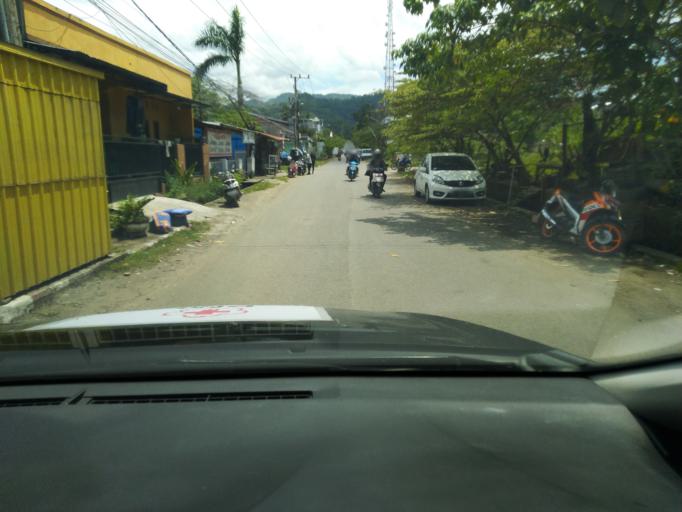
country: ID
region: Sulawesi Barat
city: Mamuju
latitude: -2.6798
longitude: 118.8829
